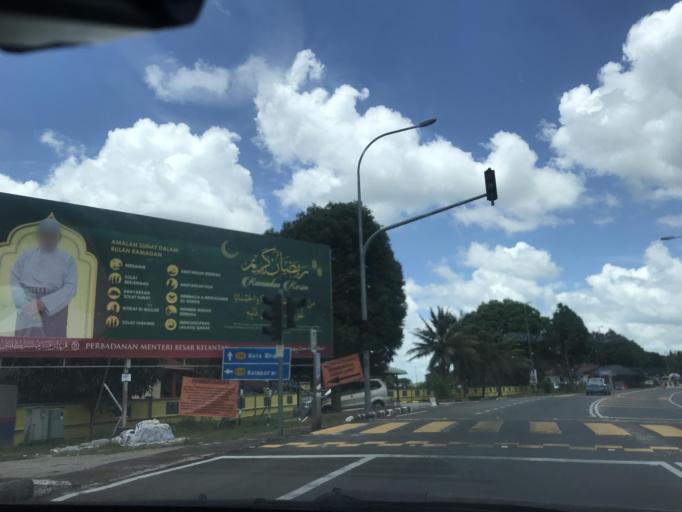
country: MY
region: Kelantan
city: Tumpat
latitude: 6.2108
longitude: 102.1108
